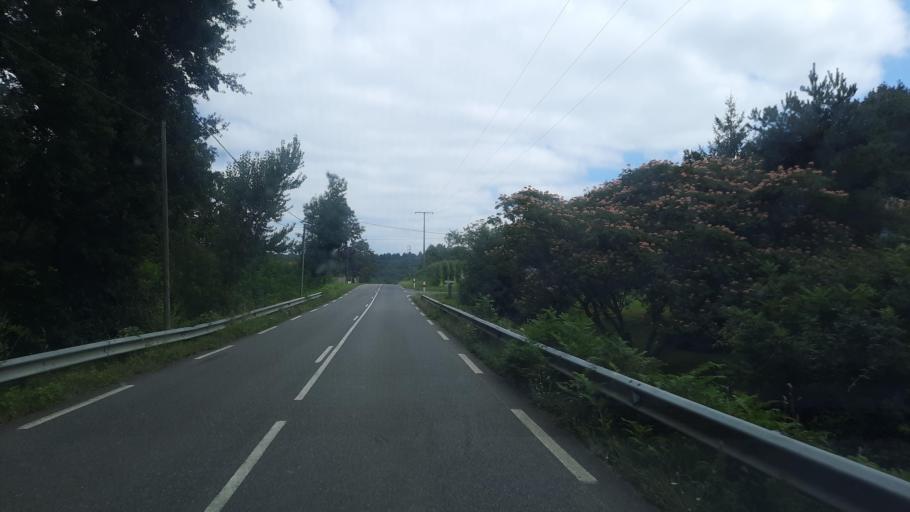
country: FR
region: Midi-Pyrenees
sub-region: Departement des Hautes-Pyrenees
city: Trie-sur-Baise
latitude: 43.2995
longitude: 0.4194
